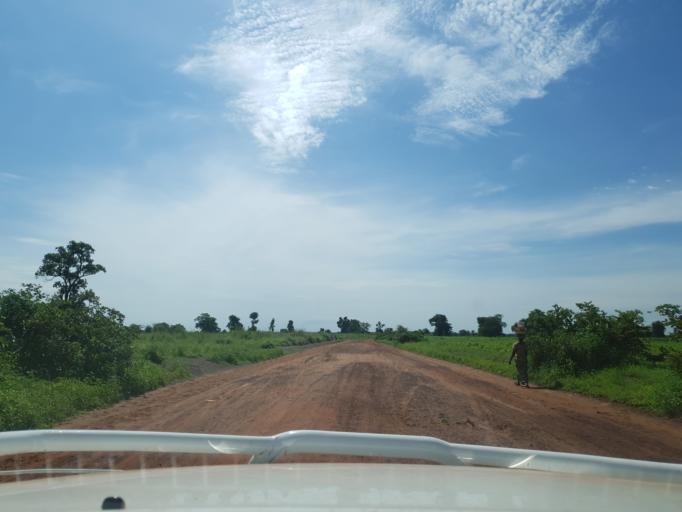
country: ML
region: Koulikoro
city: Banamba
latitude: 13.2803
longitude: -7.5524
